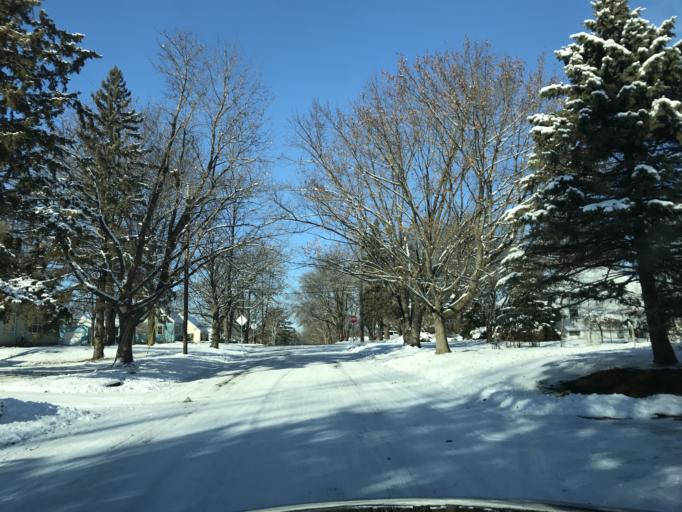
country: US
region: Wisconsin
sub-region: Dane County
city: Monona
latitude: 43.0772
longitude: -89.3185
